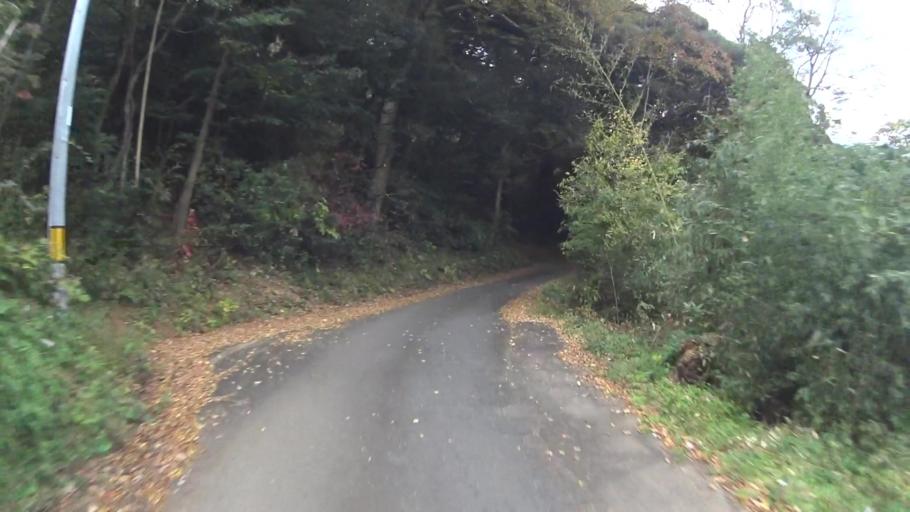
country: JP
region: Kyoto
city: Maizuru
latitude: 35.5627
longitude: 135.4627
